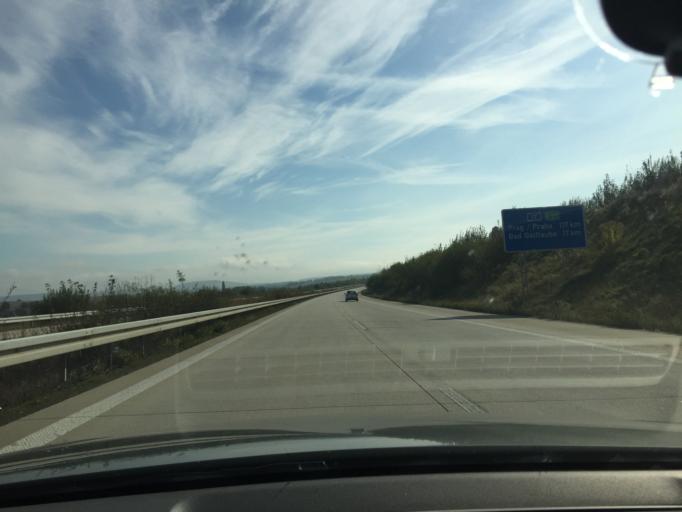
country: DE
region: Saxony
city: Dohna
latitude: 50.9393
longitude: 13.8805
